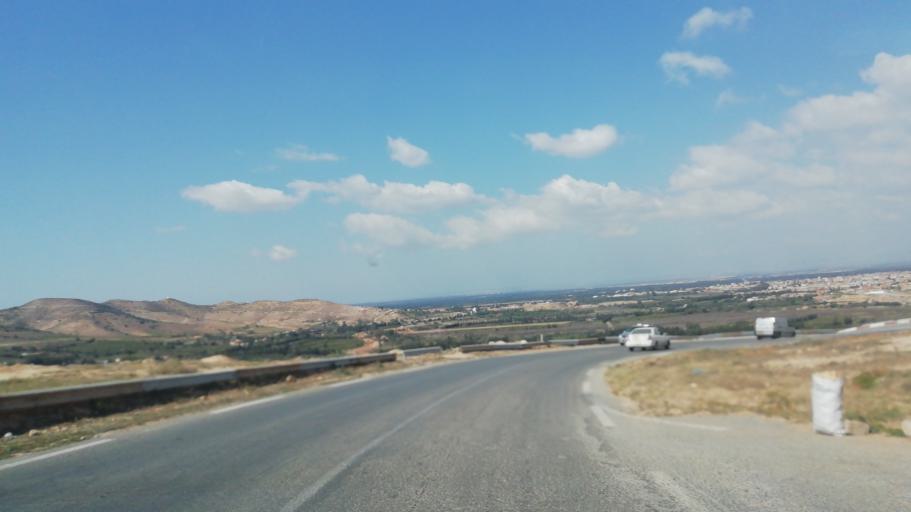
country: DZ
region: Mascara
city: Mascara
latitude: 35.5558
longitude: 0.0667
